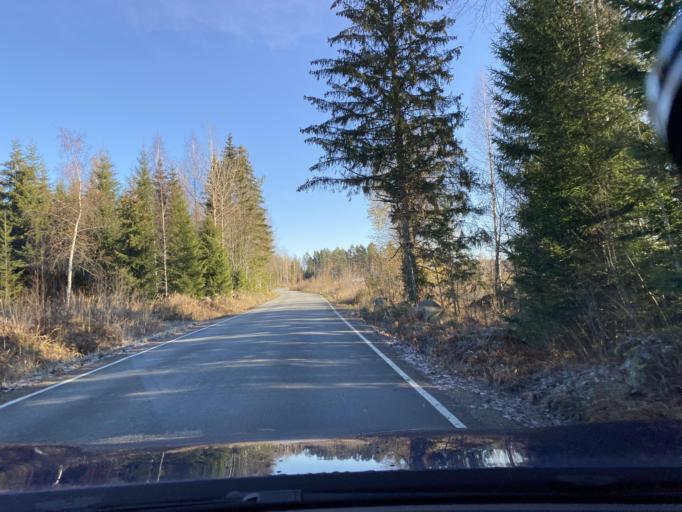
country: FI
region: Haeme
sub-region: Haemeenlinna
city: Kalvola
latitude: 61.0255
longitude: 24.1633
